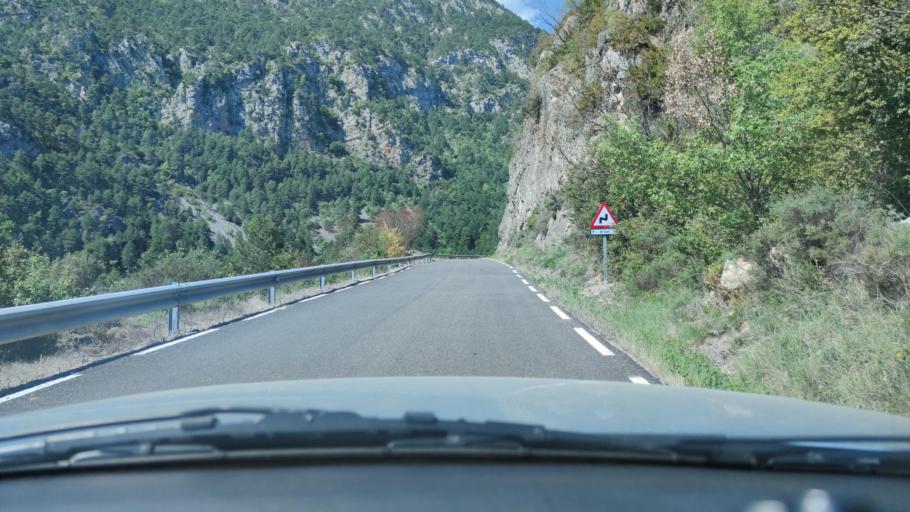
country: ES
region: Catalonia
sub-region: Provincia de Lleida
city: Coll de Nargo
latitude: 42.2919
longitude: 1.3256
